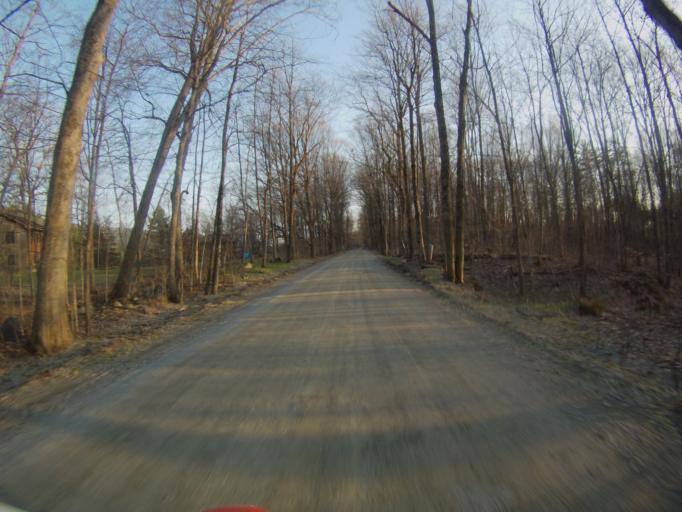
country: US
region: Vermont
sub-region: Addison County
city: Middlebury (village)
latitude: 44.0506
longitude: -73.1032
